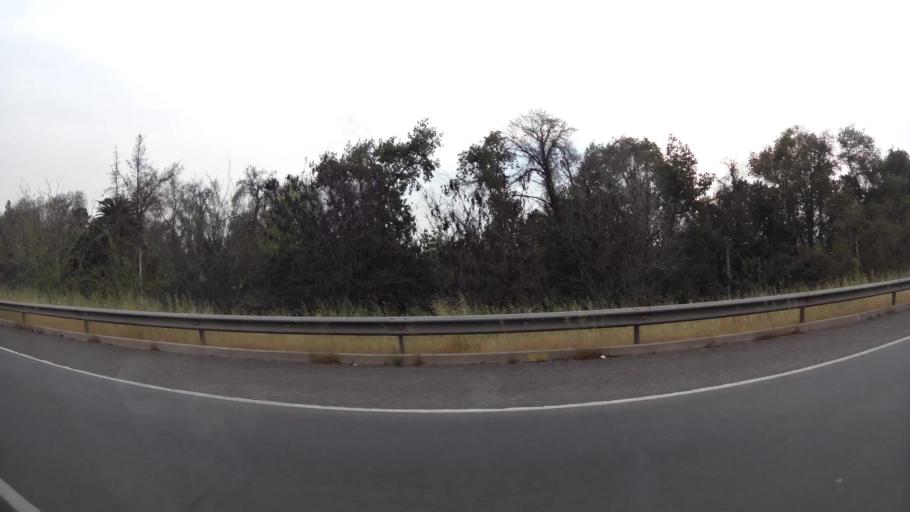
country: CL
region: Santiago Metropolitan
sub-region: Provincia de Chacabuco
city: Chicureo Abajo
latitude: -33.2428
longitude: -70.6977
